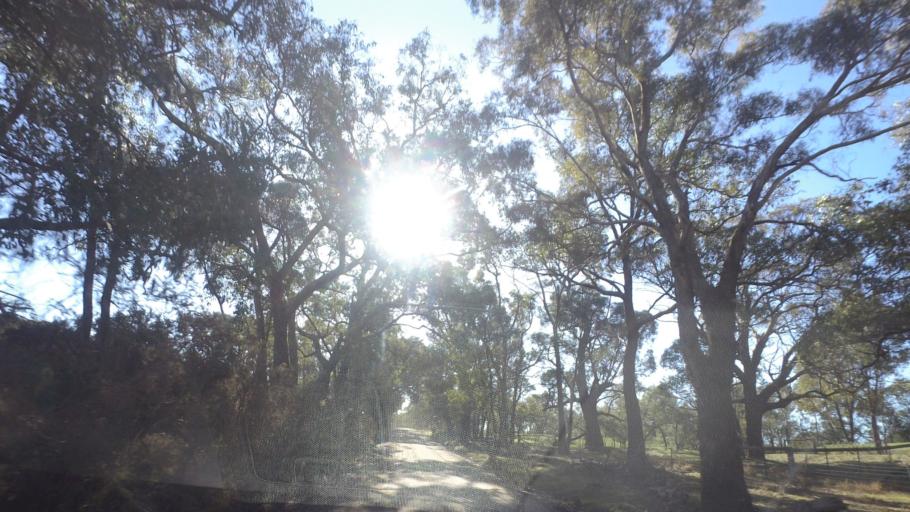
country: AU
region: Victoria
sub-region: Mount Alexander
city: Castlemaine
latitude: -37.1312
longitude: 144.4063
